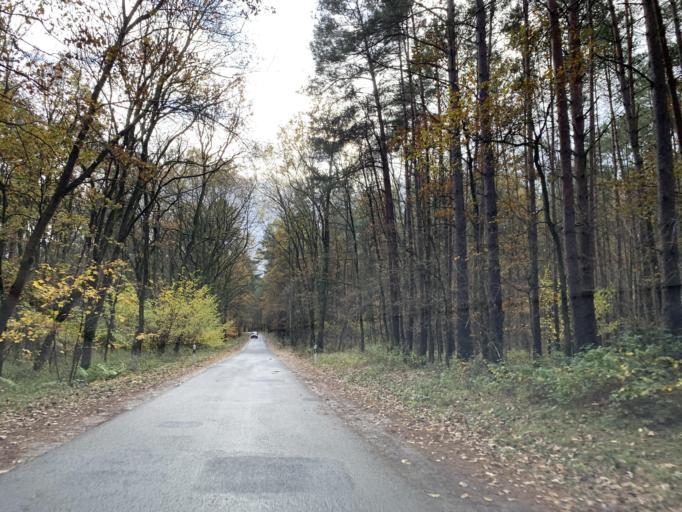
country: DE
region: Mecklenburg-Vorpommern
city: Blankensee
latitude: 53.3983
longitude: 13.2622
